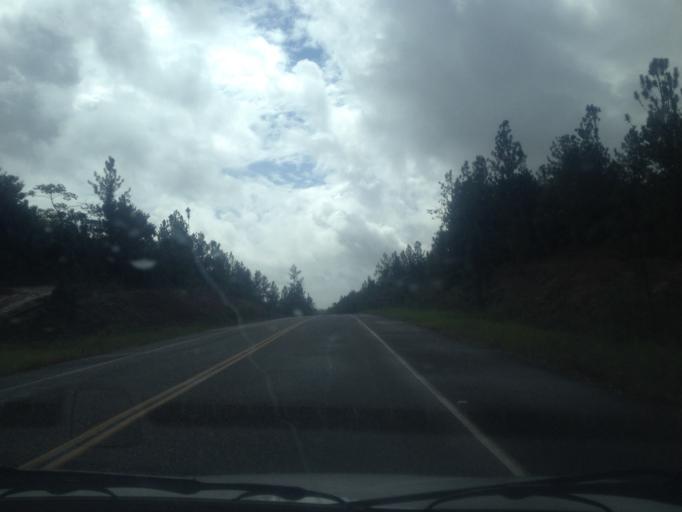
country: BR
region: Bahia
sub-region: Entre Rios
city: Entre Rios
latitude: -12.1220
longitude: -37.7889
